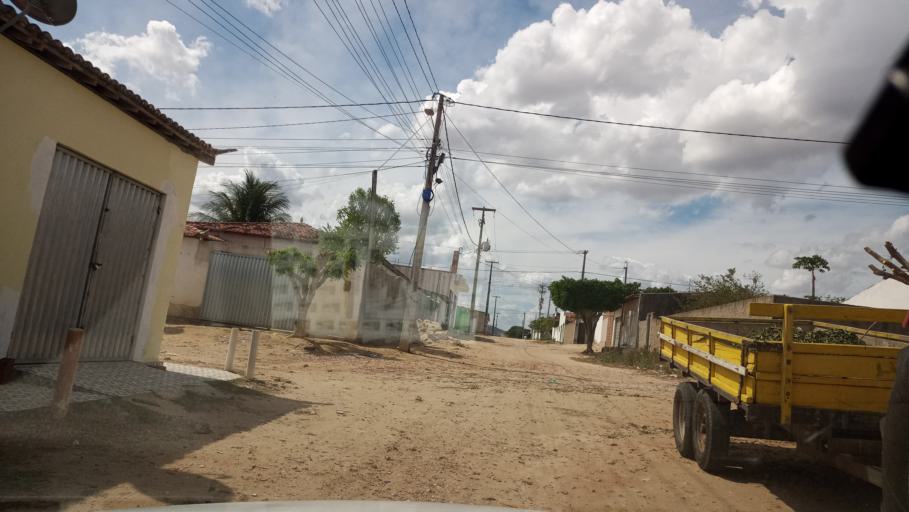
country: BR
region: Rio Grande do Norte
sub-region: Tangara
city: Tangara
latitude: -6.2049
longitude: -35.8038
